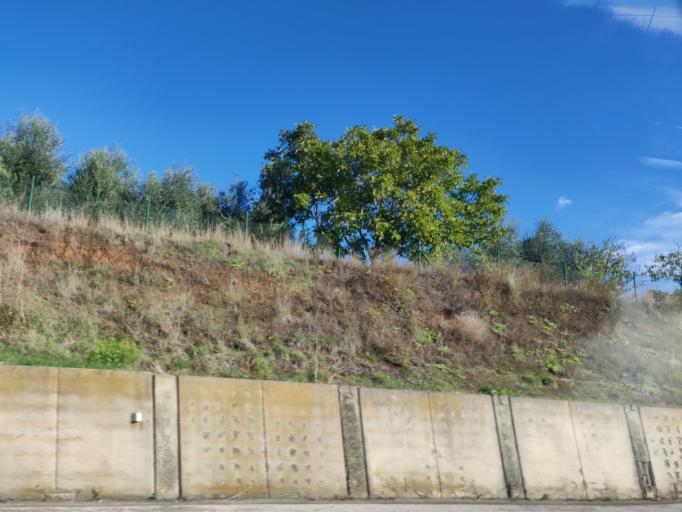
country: IT
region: Tuscany
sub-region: Provincia di Grosseto
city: Follonica
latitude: 42.9577
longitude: 10.7957
